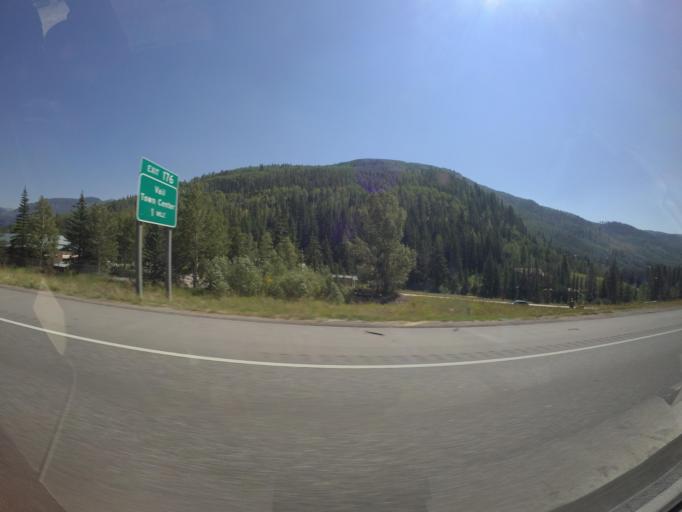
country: US
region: Colorado
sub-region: Eagle County
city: Vail
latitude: 39.6411
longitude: -106.3979
